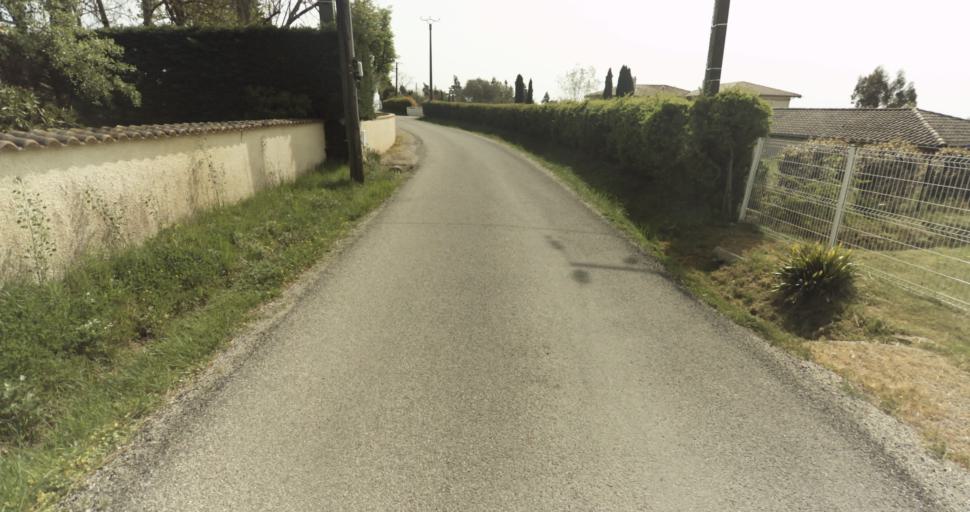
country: FR
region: Midi-Pyrenees
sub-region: Departement du Tarn-et-Garonne
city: Moissac
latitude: 44.1071
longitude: 1.0765
